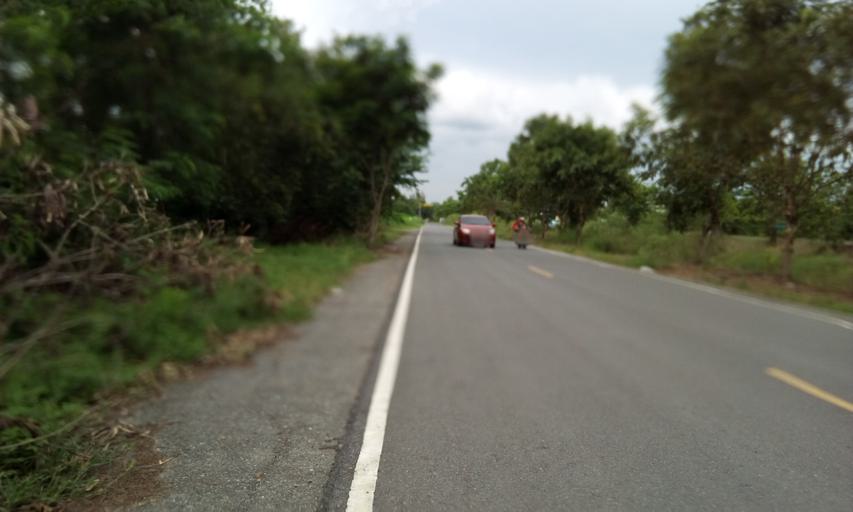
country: TH
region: Pathum Thani
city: Nong Suea
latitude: 14.2371
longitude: 100.8229
